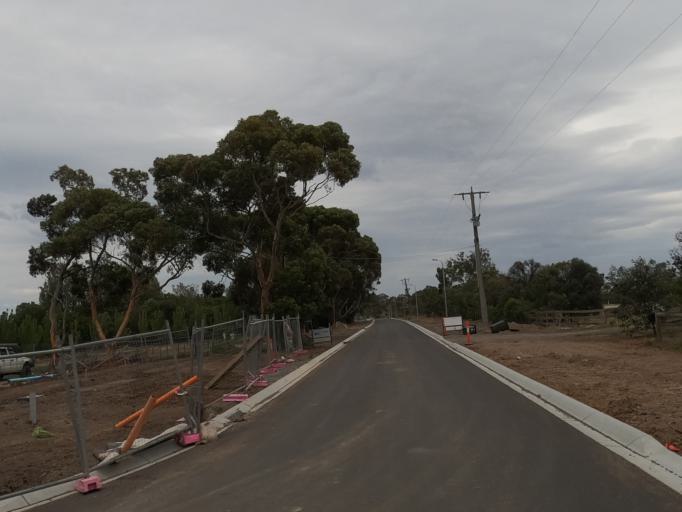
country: AU
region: Victoria
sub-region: Hume
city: Greenvale
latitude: -37.6427
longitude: 144.8712
